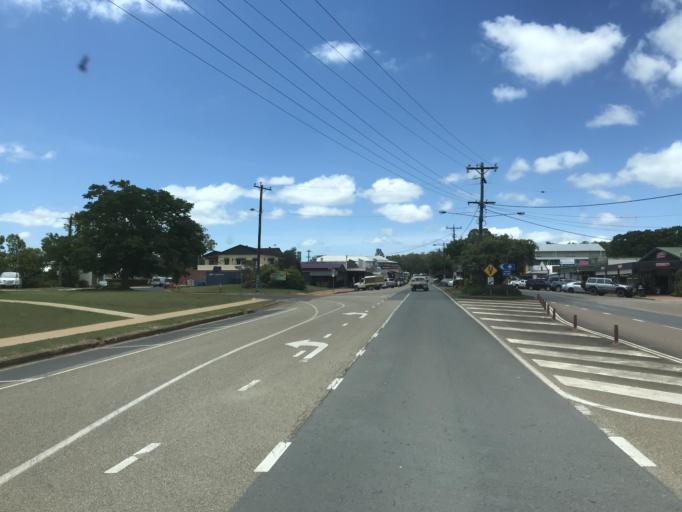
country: AU
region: Queensland
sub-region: Tablelands
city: Ravenshoe
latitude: -17.6082
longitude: 145.4833
